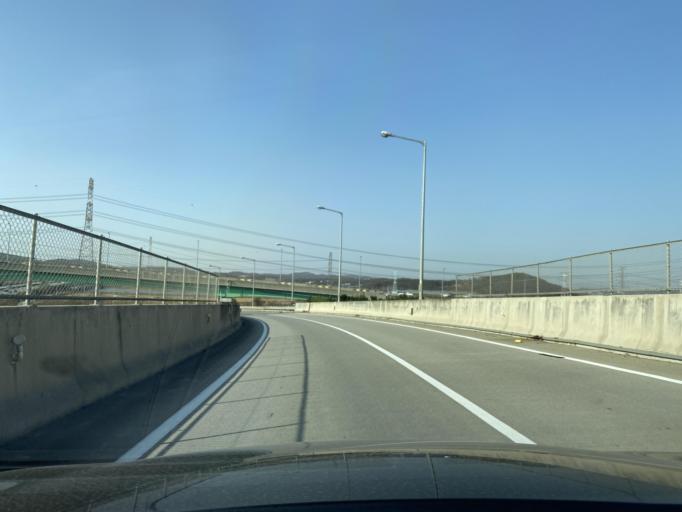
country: KR
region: Gyeonggi-do
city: Hwaseong-si
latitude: 37.0554
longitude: 126.8888
